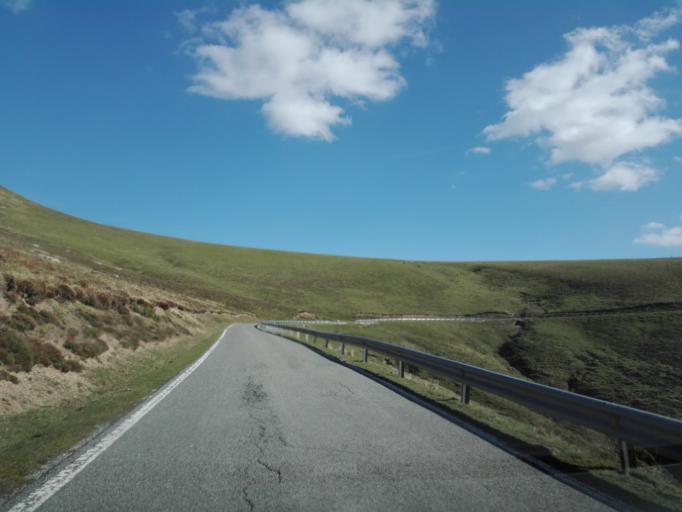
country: ES
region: Navarre
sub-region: Provincia de Navarra
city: Garaioa
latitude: 42.9599
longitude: -1.1389
